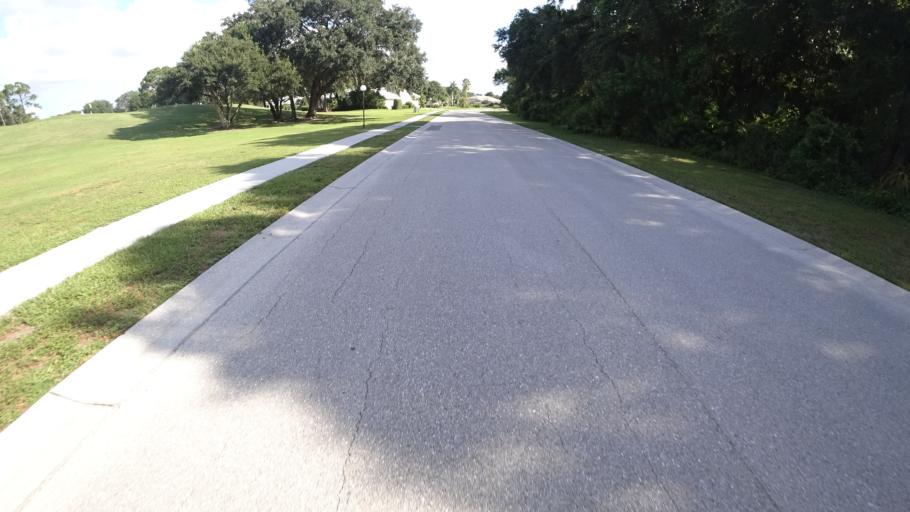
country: US
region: Florida
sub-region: Sarasota County
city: Desoto Lakes
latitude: 27.4036
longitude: -82.4831
